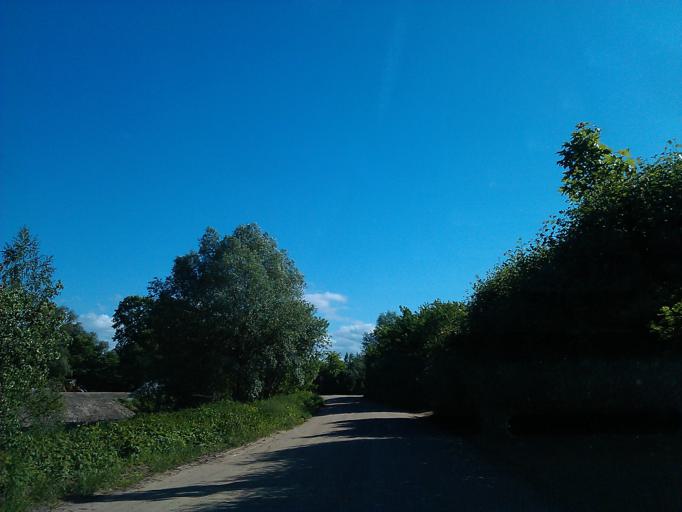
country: LV
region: Adazi
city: Adazi
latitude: 57.0884
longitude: 24.3210
